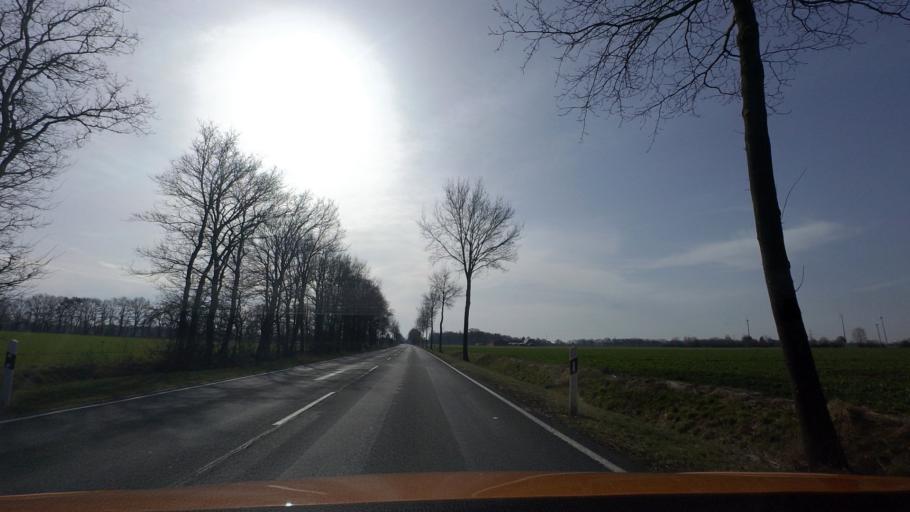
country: DE
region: Lower Saxony
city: Raddestorf
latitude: 52.4200
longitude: 8.9482
